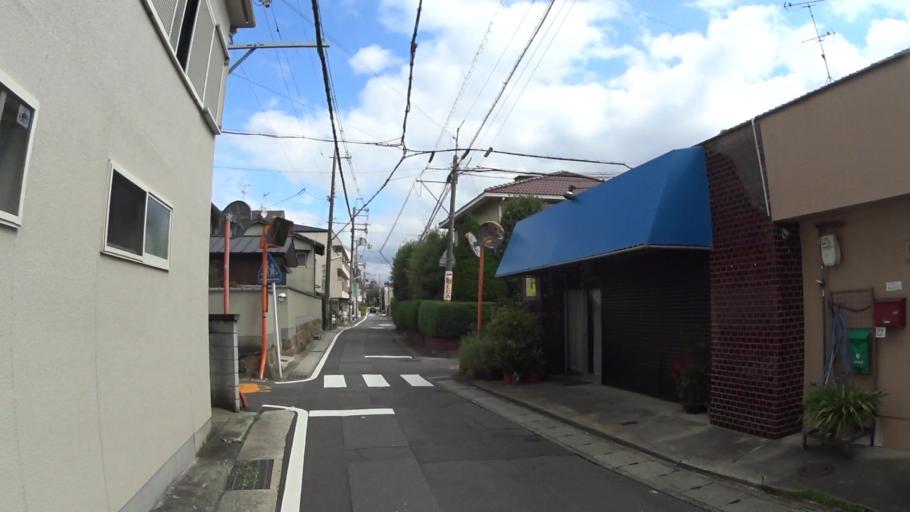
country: JP
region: Kyoto
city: Muko
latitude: 34.9602
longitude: 135.7199
